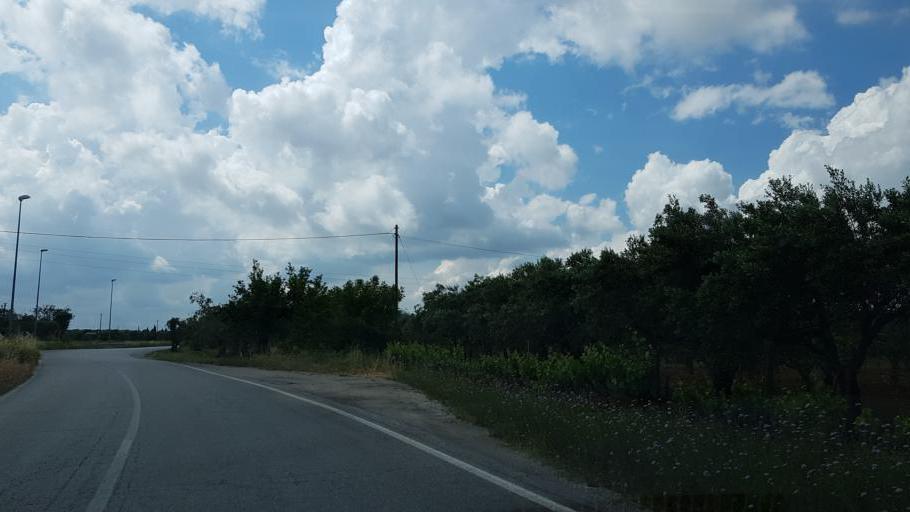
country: IT
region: Apulia
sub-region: Provincia di Brindisi
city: Mesagne
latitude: 40.5390
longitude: 17.8173
